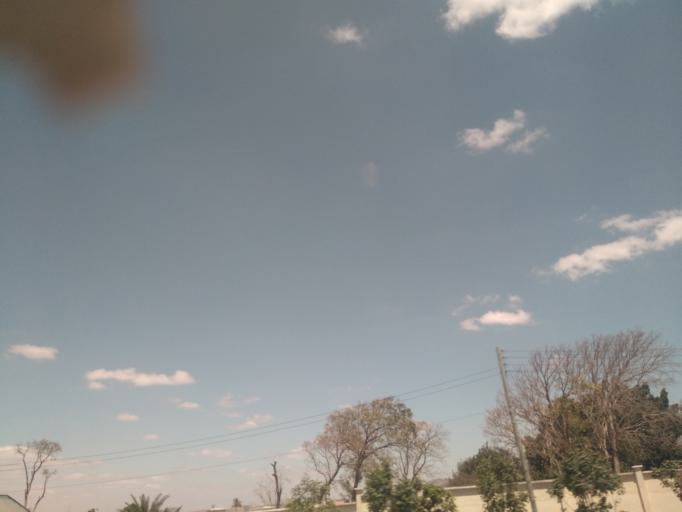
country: TZ
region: Dodoma
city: Dodoma
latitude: -6.1803
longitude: 35.7335
